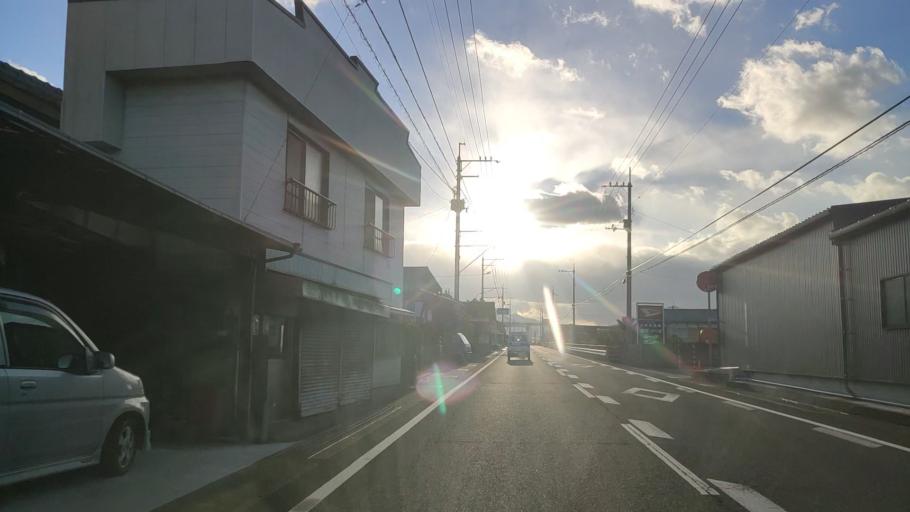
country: JP
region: Ehime
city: Saijo
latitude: 33.8931
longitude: 133.0923
